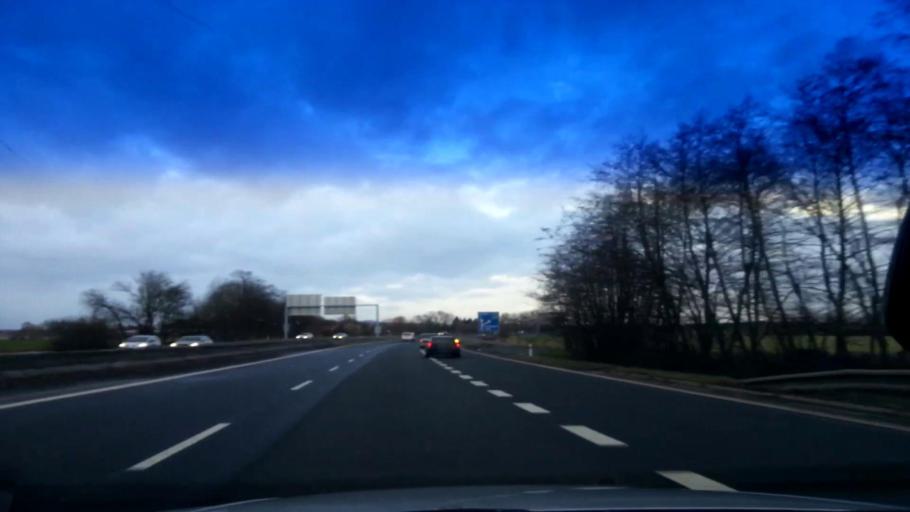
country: CZ
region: Karlovarsky
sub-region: Okres Cheb
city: Cheb
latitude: 50.0999
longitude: 12.3665
